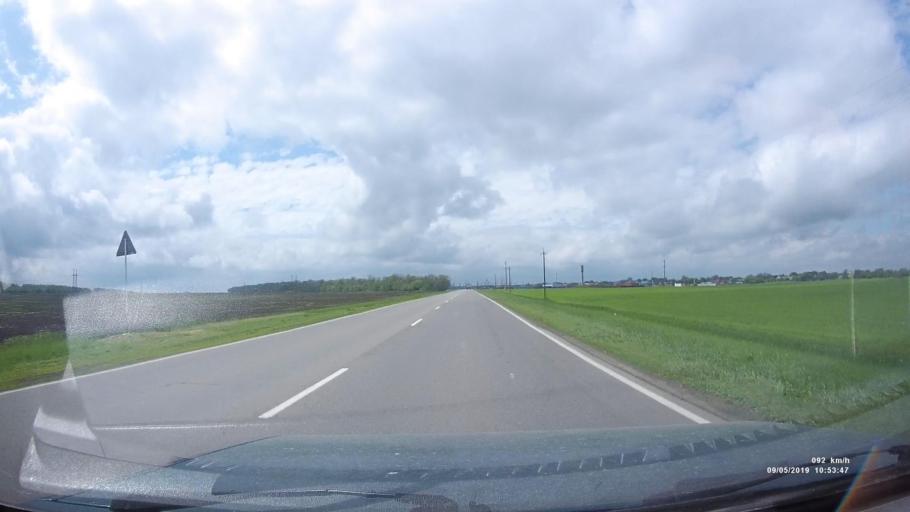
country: RU
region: Rostov
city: Peshkovo
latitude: 46.8841
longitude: 39.3373
